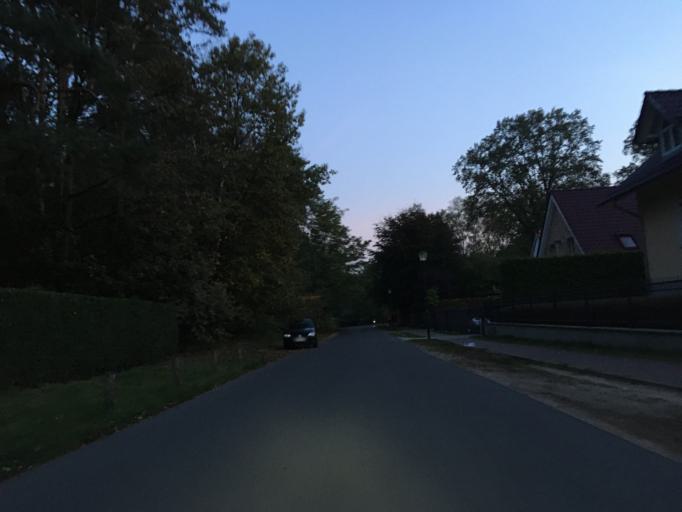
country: DE
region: Brandenburg
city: Birkenwerder
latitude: 52.6755
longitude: 13.3233
